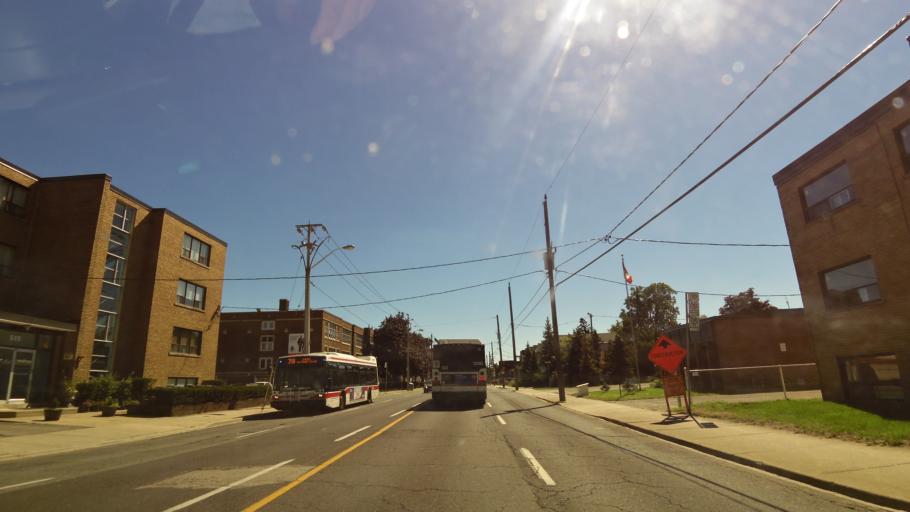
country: CA
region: Ontario
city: Etobicoke
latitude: 43.6647
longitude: -79.4908
